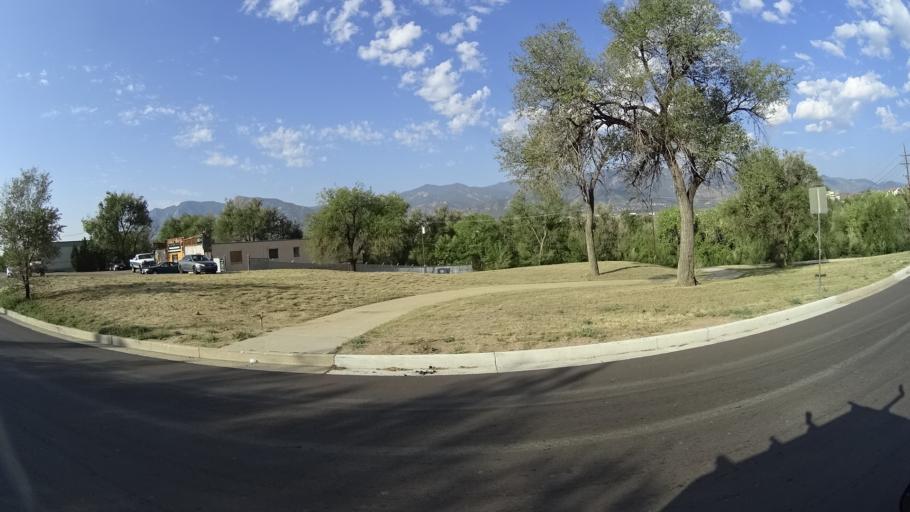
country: US
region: Colorado
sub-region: El Paso County
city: Colorado Springs
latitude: 38.8198
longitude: -104.8154
